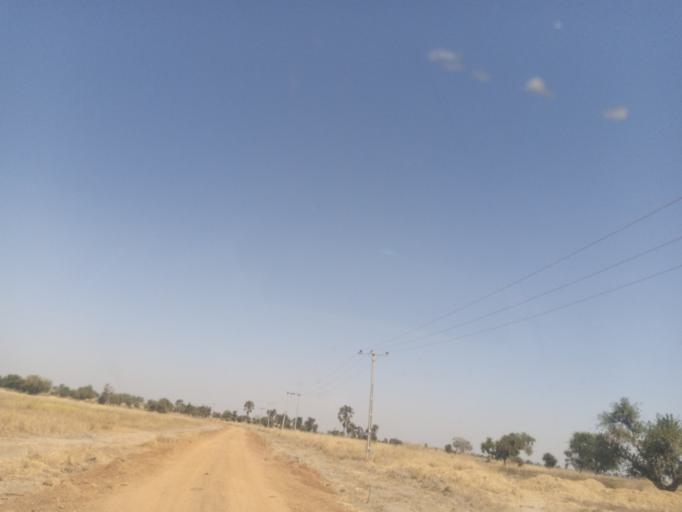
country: NG
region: Adamawa
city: Yola
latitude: 9.3017
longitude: 12.8890
